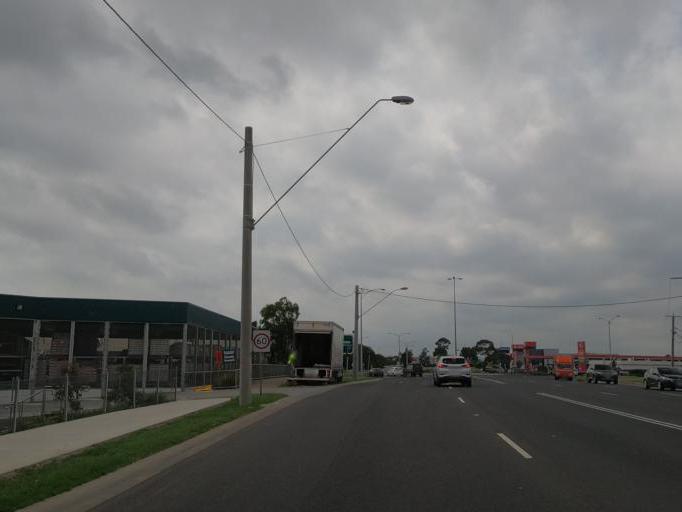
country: AU
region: Victoria
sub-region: Whittlesea
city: Thomastown
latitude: -37.6939
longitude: 145.0240
